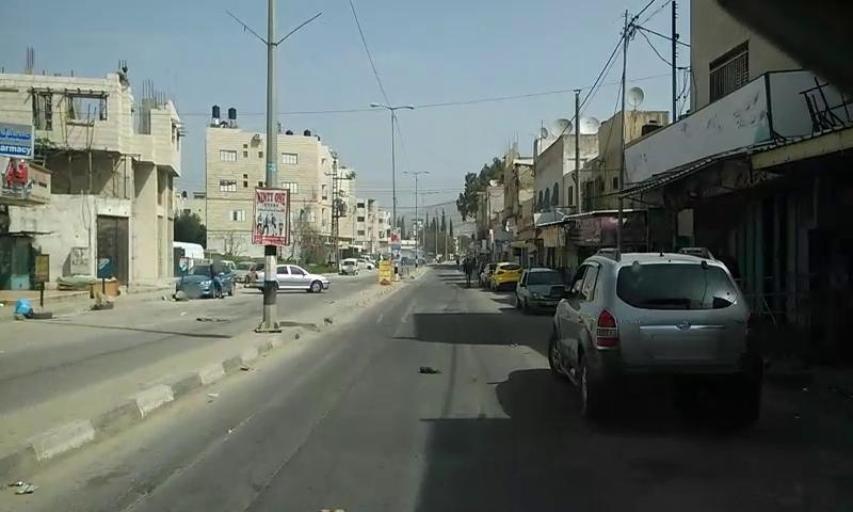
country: PS
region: West Bank
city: `Azmut
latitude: 32.2217
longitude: 35.2978
